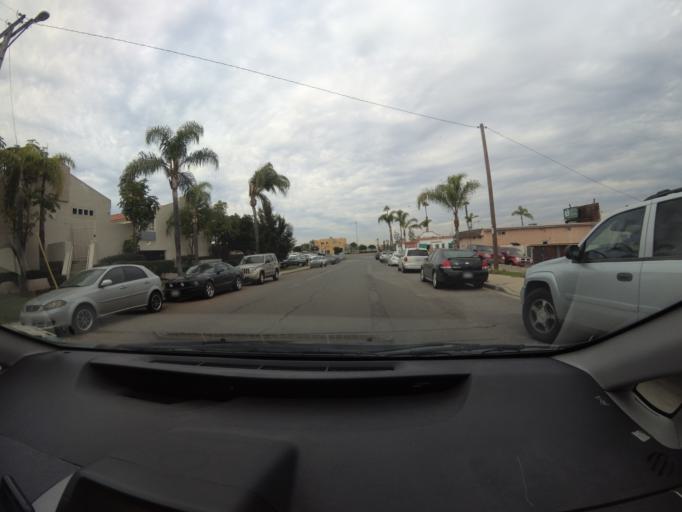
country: US
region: California
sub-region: San Diego County
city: Imperial Beach
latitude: 32.5829
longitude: -117.1044
